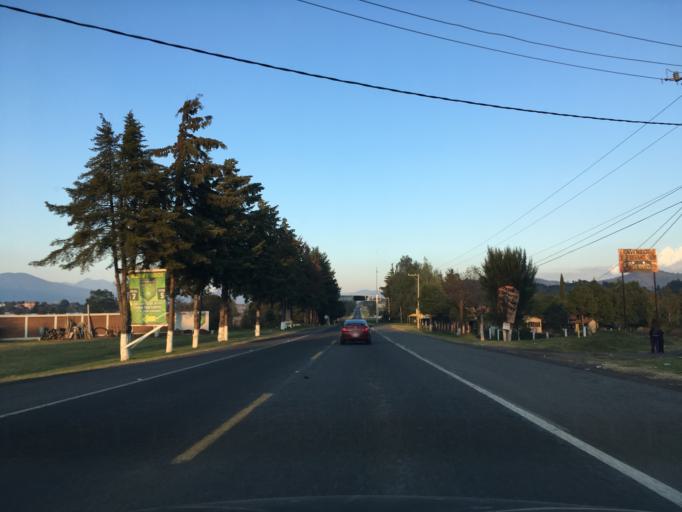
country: MX
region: Michoacan
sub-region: Patzcuaro
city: Santa Ana Chapitiro
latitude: 19.5243
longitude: -101.6485
